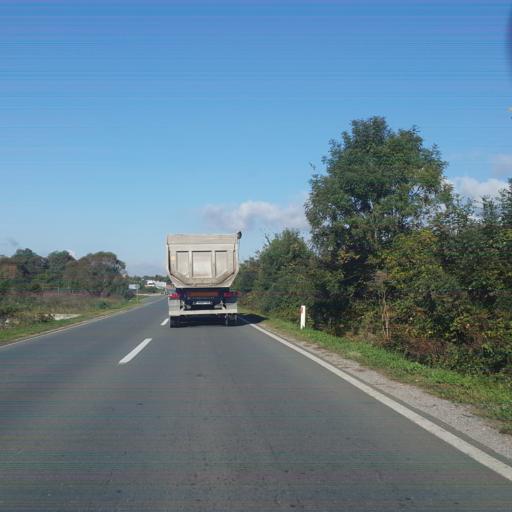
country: RS
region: Central Serbia
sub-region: Rasinski Okrug
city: Trstenik
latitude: 43.6302
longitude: 20.9687
